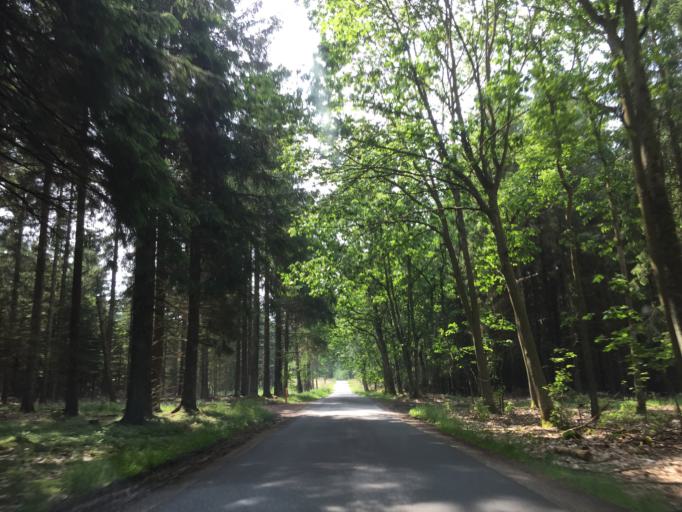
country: DK
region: Central Jutland
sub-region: Silkeborg Kommune
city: Virklund
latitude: 56.0722
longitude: 9.4704
